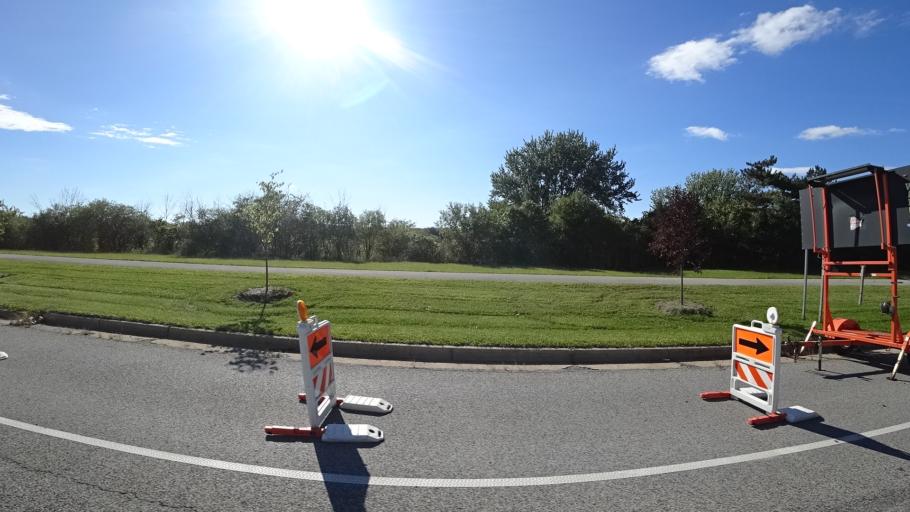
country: US
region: Illinois
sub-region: Cook County
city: Oak Forest
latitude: 41.5916
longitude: -87.7360
